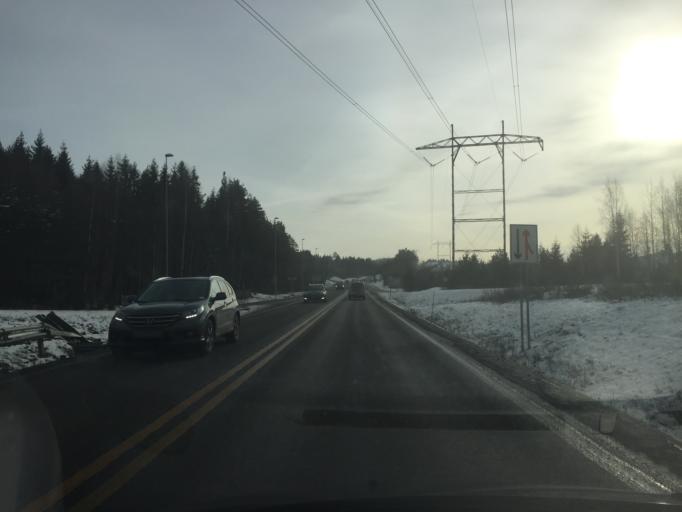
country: NO
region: Hedmark
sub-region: Loten
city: Loten
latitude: 60.7865
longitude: 11.3029
